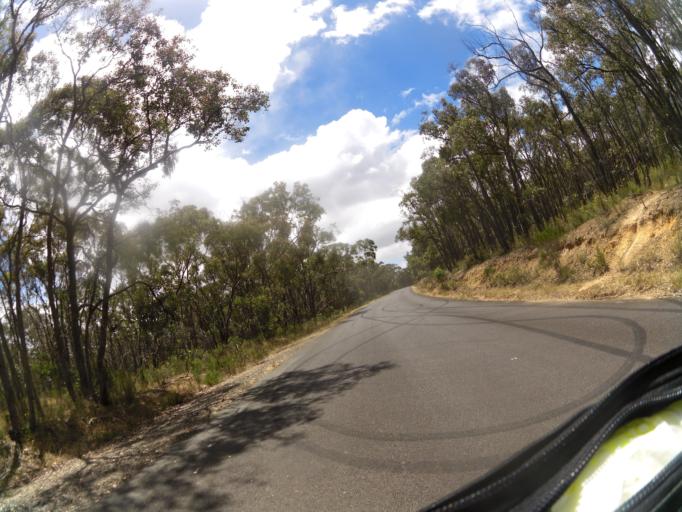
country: AU
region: Victoria
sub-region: Mount Alexander
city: Castlemaine
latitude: -37.0218
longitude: 144.2432
